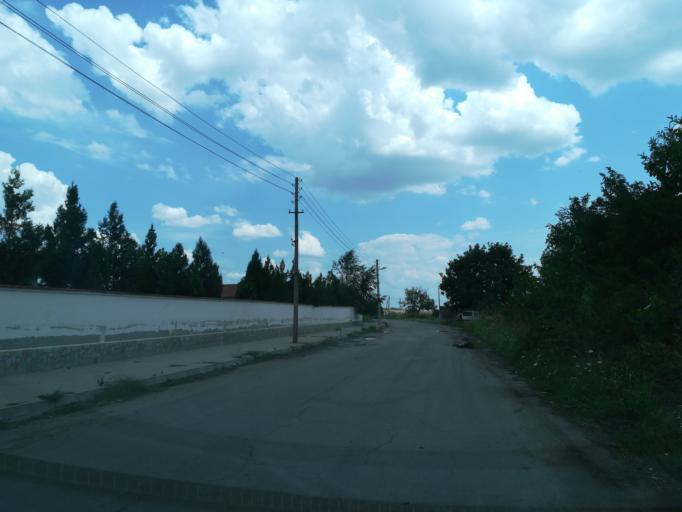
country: BG
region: Khaskovo
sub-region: Obshtina Mineralni Bani
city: Mineralni Bani
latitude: 41.9856
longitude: 25.1733
